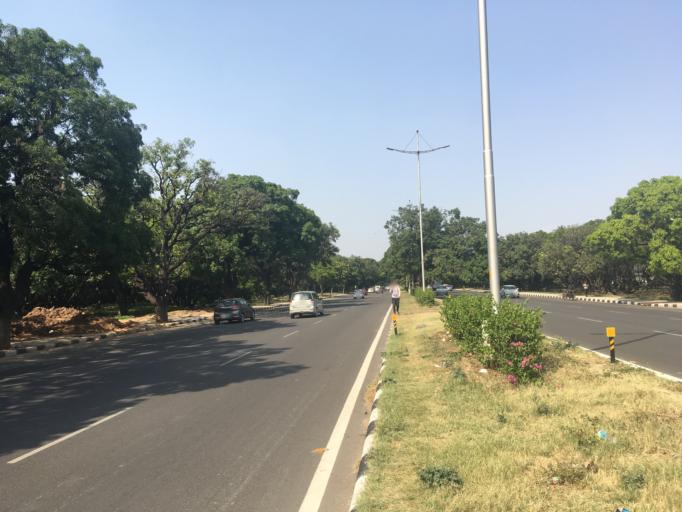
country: IN
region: Chandigarh
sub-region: Chandigarh
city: Chandigarh
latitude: 30.7084
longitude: 76.7971
